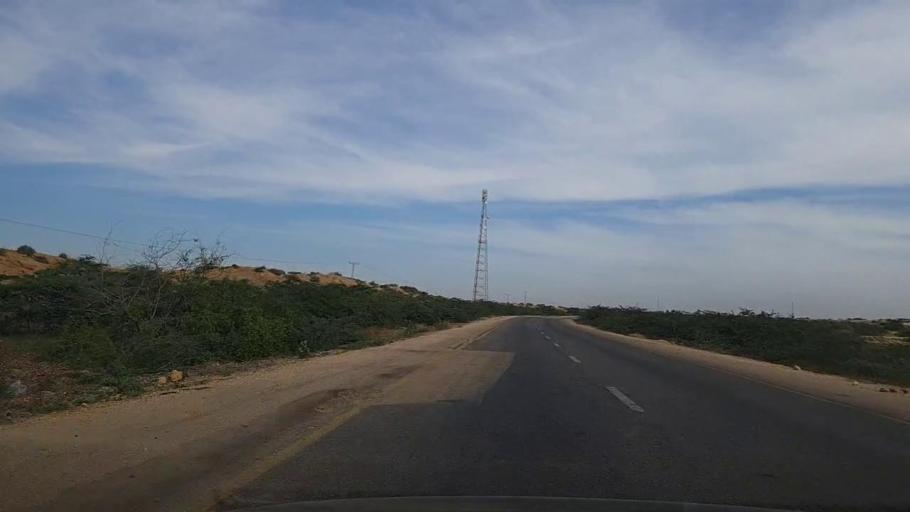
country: PK
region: Sindh
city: Thatta
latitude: 24.8622
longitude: 68.0251
